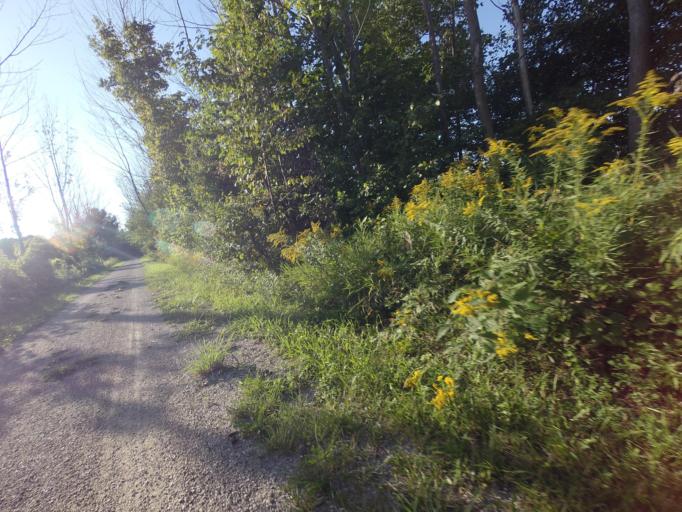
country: CA
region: Ontario
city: Goderich
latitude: 43.7574
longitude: -81.6832
